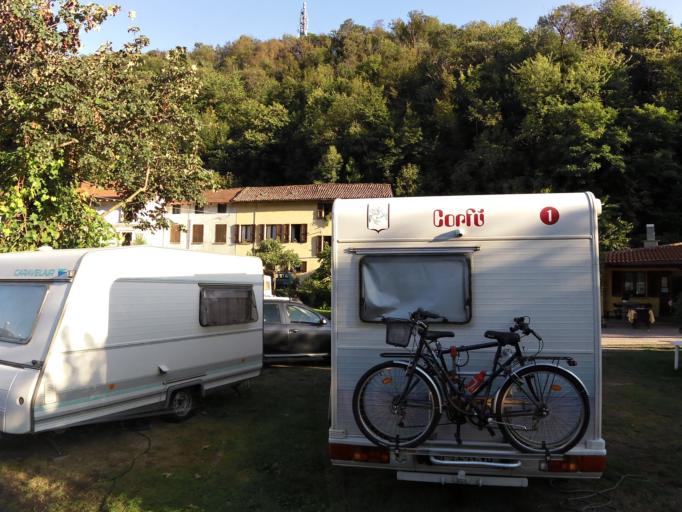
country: IT
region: Lombardy
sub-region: Provincia di Como
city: Lenno
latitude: 45.9693
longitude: 9.1927
